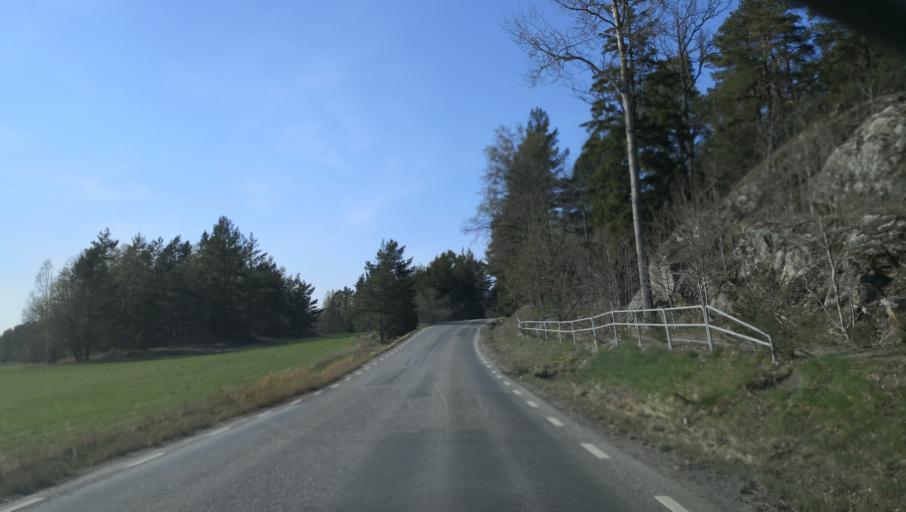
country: SE
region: Stockholm
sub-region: Varmdo Kommun
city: Hemmesta
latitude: 59.3222
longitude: 18.5521
